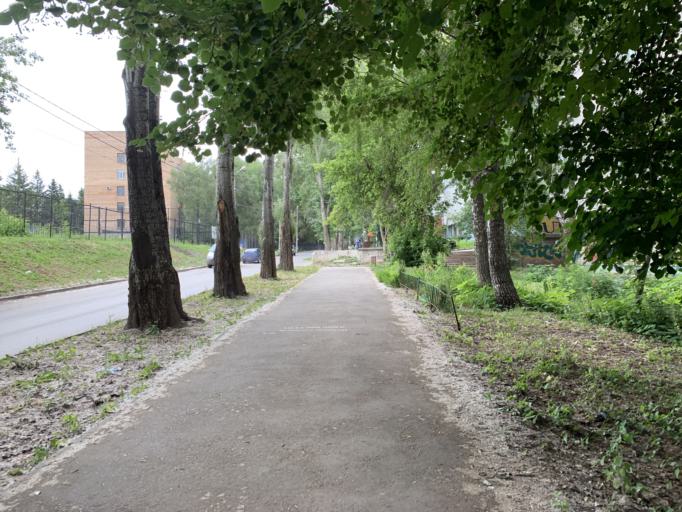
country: RU
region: Samara
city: Samara
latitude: 53.2138
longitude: 50.1727
